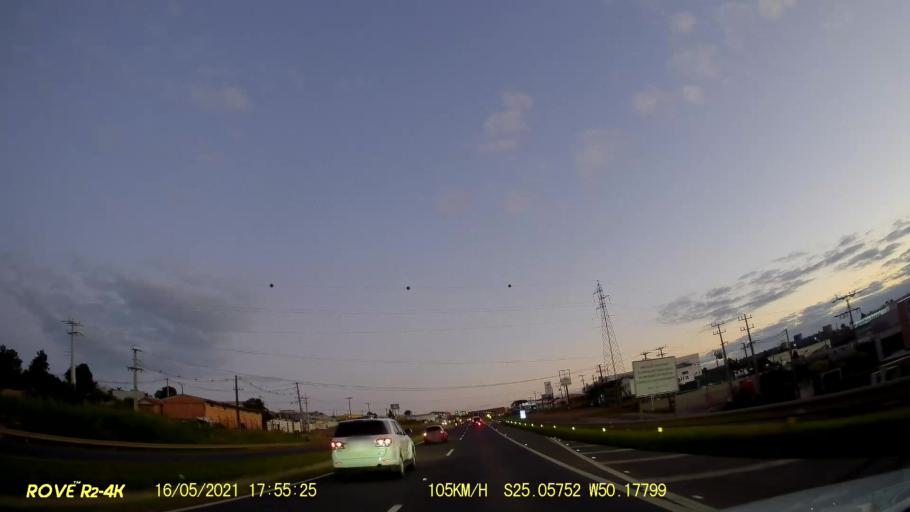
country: BR
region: Parana
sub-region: Ponta Grossa
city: Ponta Grossa
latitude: -25.0576
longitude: -50.1779
